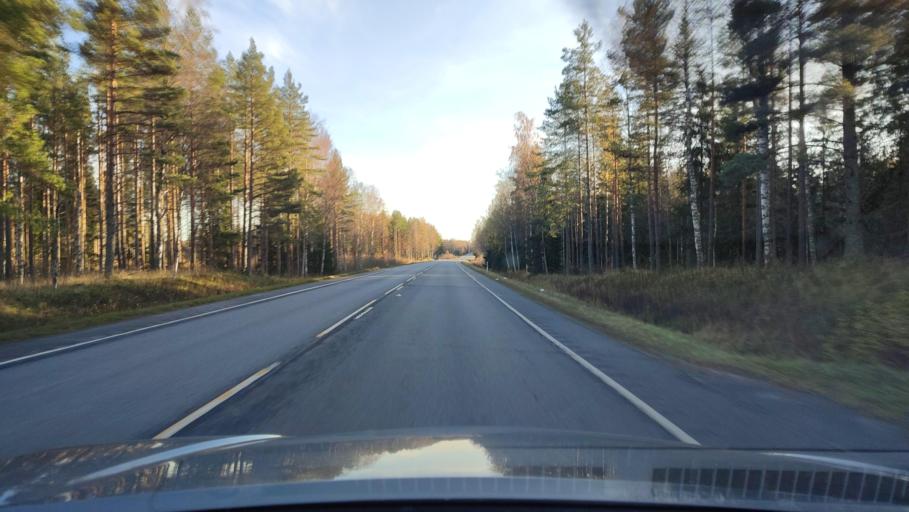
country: FI
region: Ostrobothnia
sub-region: Vaasa
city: Ristinummi
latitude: 63.0123
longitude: 21.7612
